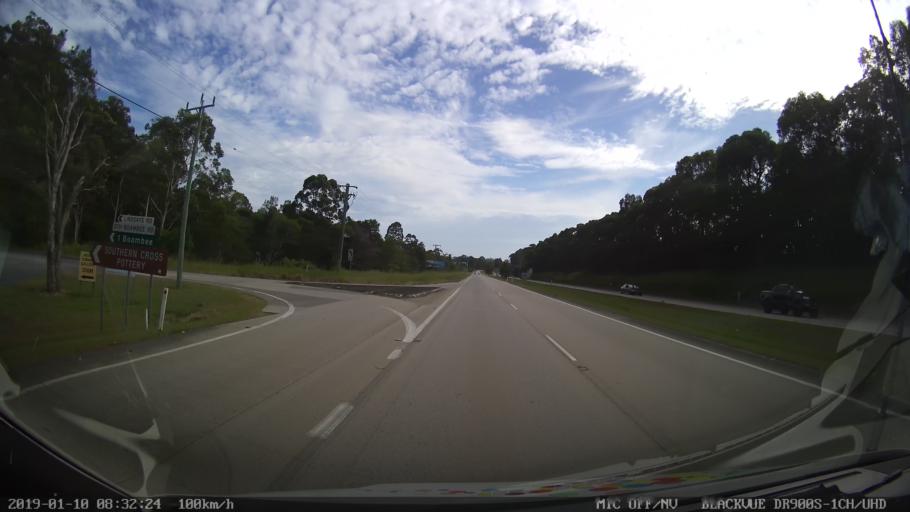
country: AU
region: New South Wales
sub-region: Coffs Harbour
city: Boambee
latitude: -30.3441
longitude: 153.0697
